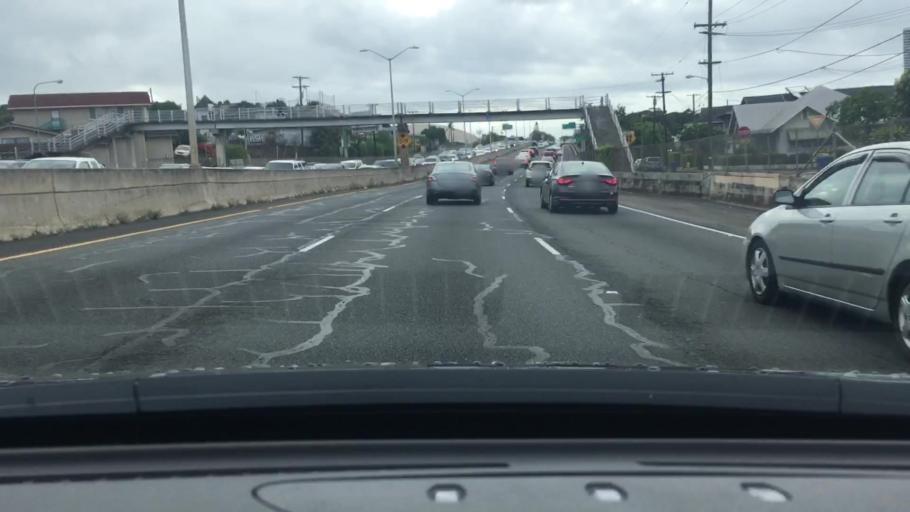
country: US
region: Hawaii
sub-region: Honolulu County
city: Honolulu
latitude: 21.2964
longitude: -157.8248
